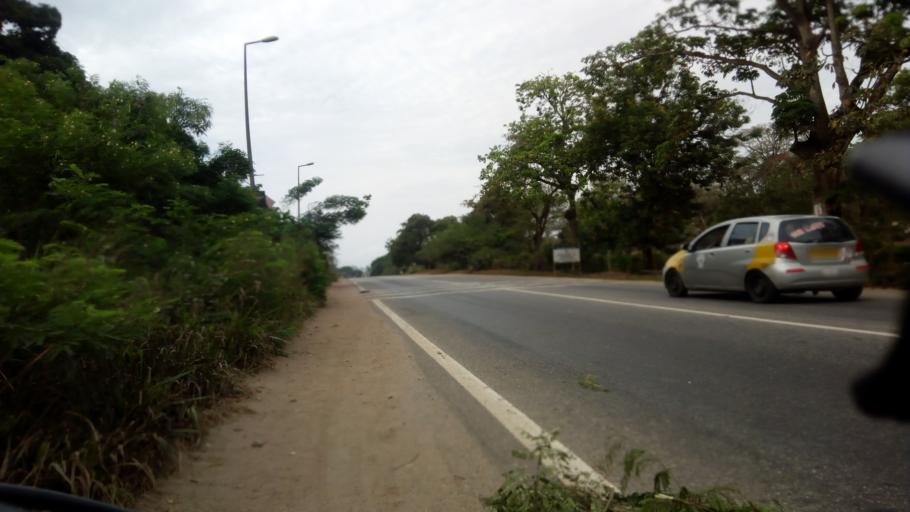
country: GH
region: Central
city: Cape Coast
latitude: 5.1112
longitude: -1.2791
